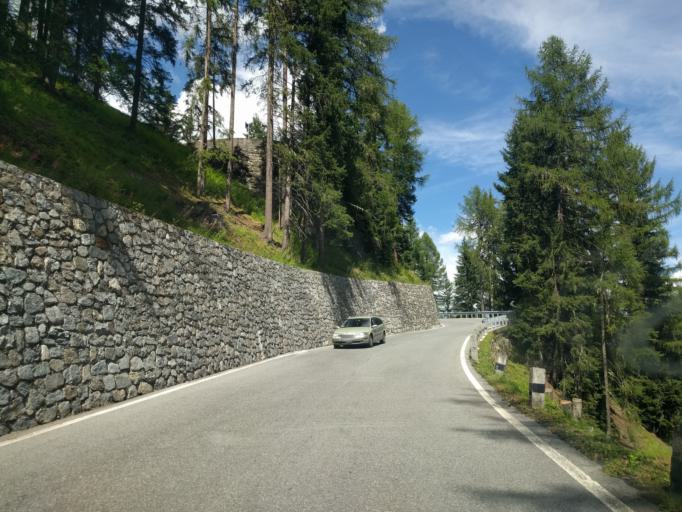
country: IT
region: Trentino-Alto Adige
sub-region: Bolzano
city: Stelvio
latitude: 46.5405
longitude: 10.5029
